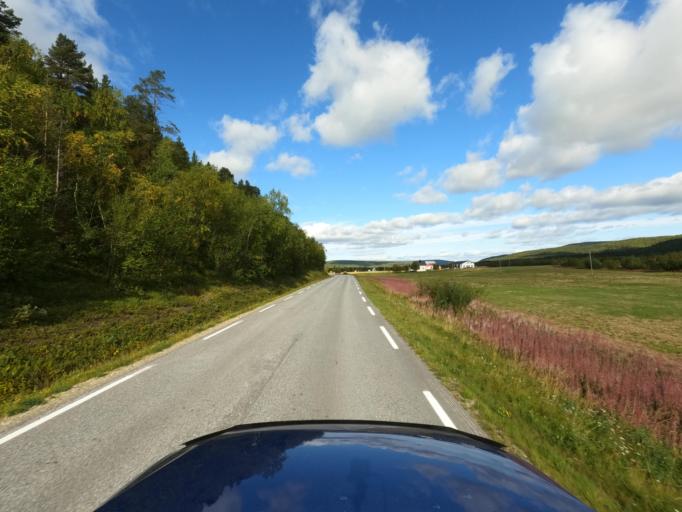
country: NO
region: Finnmark Fylke
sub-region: Karasjok
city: Karasjohka
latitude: 69.4087
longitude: 25.8064
